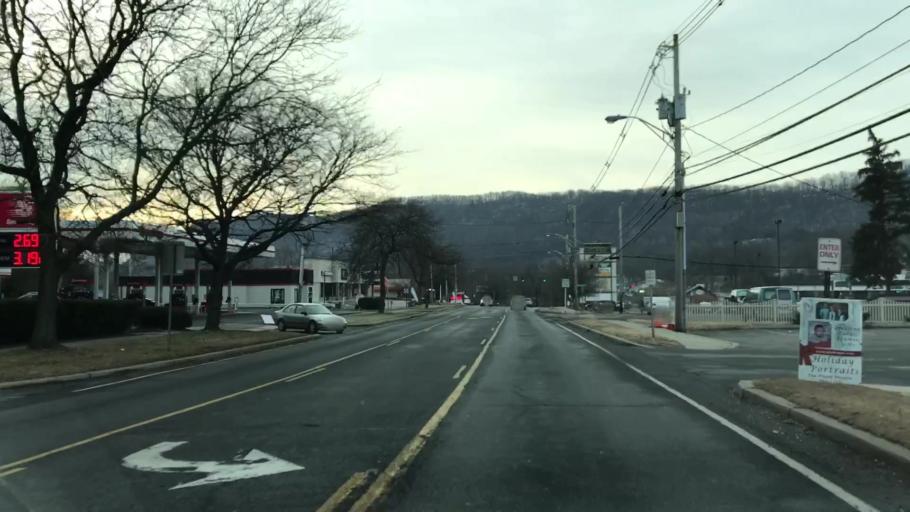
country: US
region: New York
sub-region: Rockland County
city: West Haverstraw
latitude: 41.2079
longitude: -73.9850
